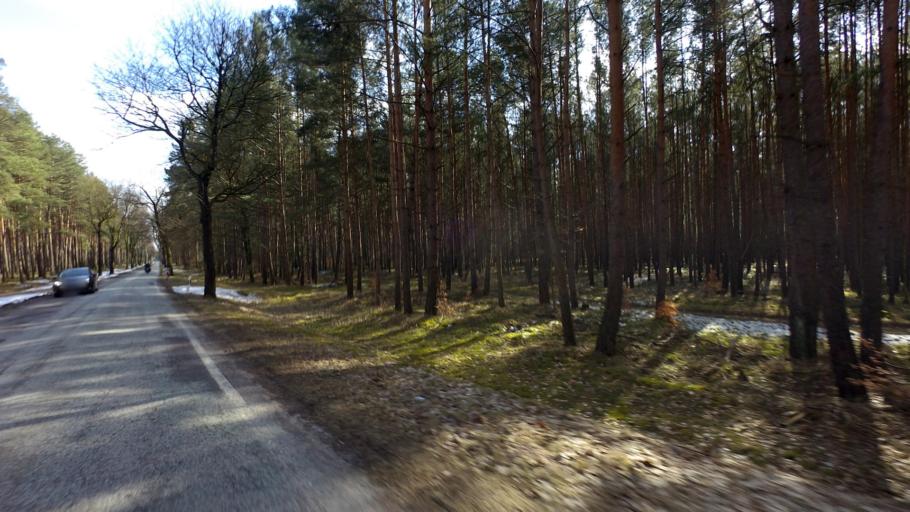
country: DE
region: Brandenburg
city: Biesenthal
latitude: 52.7896
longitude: 13.6048
